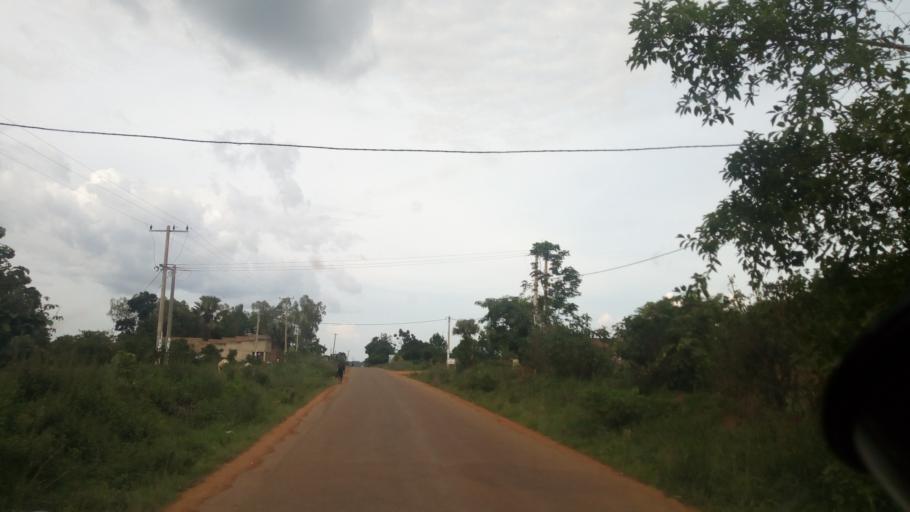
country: UG
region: Northern Region
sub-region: Lira District
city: Lira
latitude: 2.2555
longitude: 32.8474
